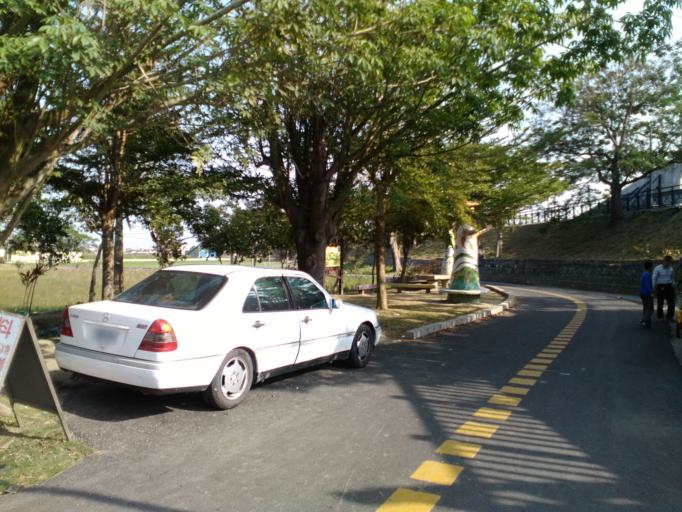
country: TW
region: Taiwan
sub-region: Chiayi
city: Taibao
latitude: 23.5700
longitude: 120.3132
